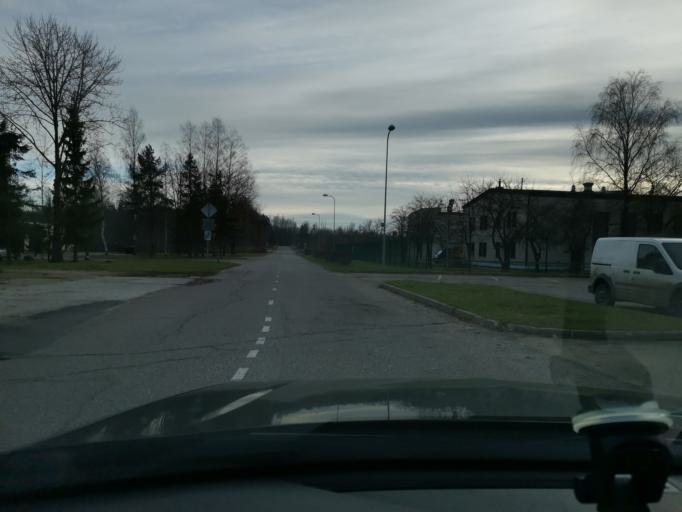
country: EE
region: Ida-Virumaa
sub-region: Sillamaee linn
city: Sillamae
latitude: 59.2738
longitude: 27.9110
